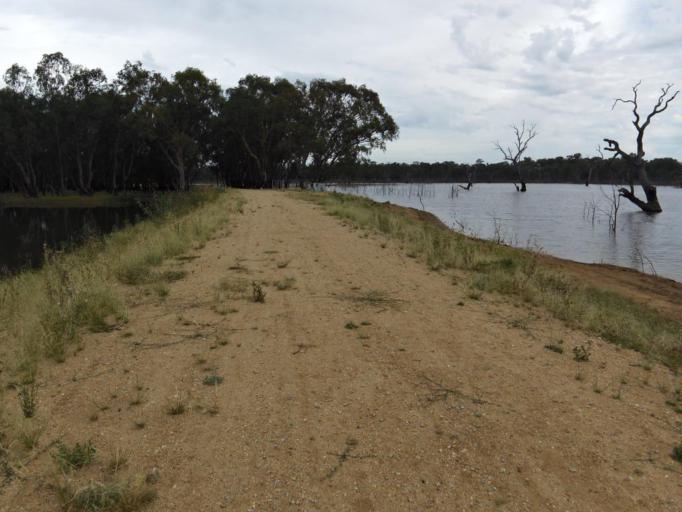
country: AU
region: Victoria
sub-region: Greater Bendigo
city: Kennington
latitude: -36.8695
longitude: 144.6251
